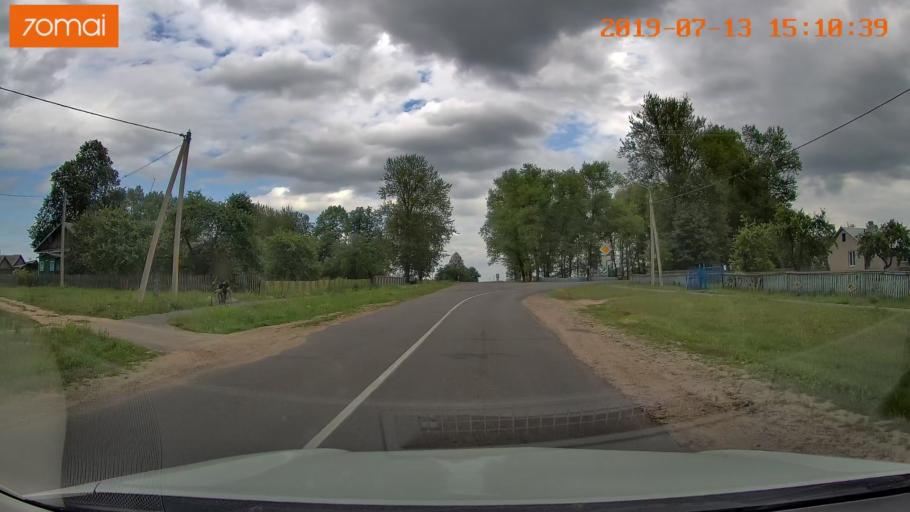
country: BY
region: Mogilev
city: Hlusha
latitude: 53.1694
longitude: 28.7774
